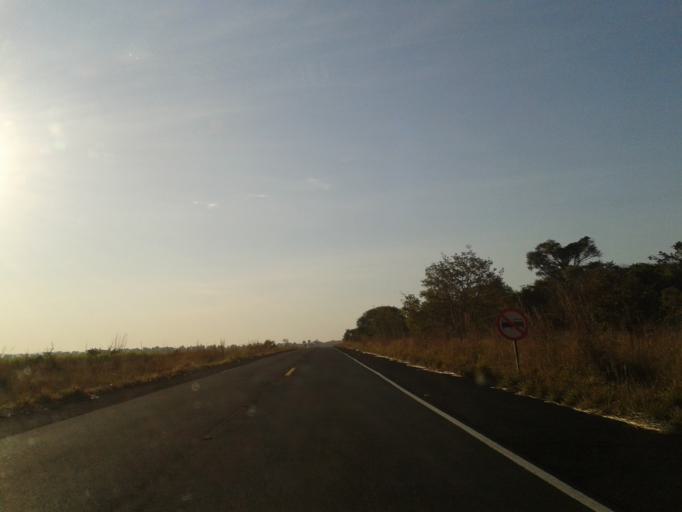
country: BR
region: Minas Gerais
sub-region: Santa Vitoria
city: Santa Vitoria
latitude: -19.1476
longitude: -50.1680
